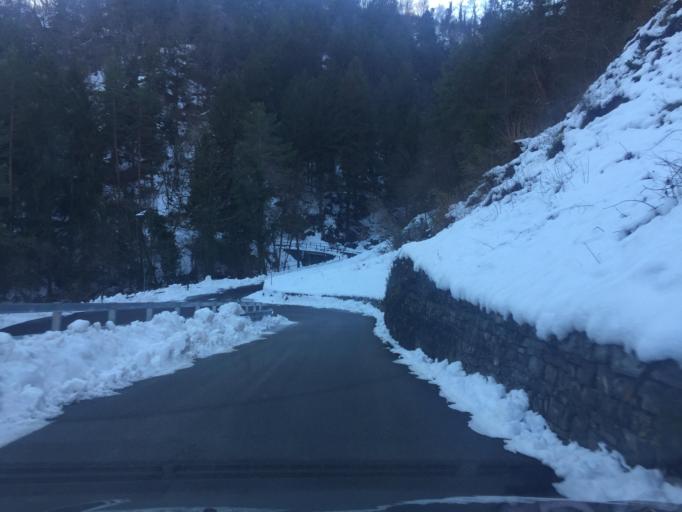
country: IT
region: Friuli Venezia Giulia
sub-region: Provincia di Udine
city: Tolmezzo
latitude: 46.4179
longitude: 13.0044
